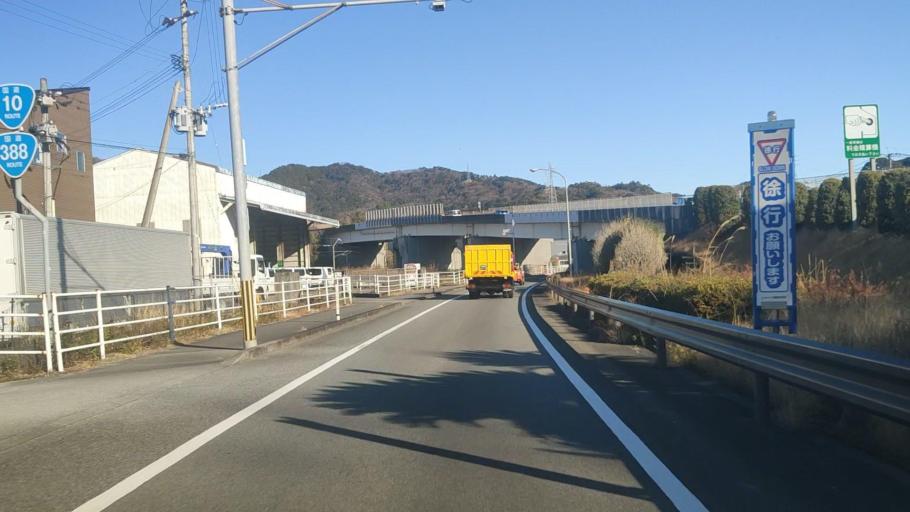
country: JP
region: Miyazaki
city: Nobeoka
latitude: 32.4968
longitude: 131.6623
